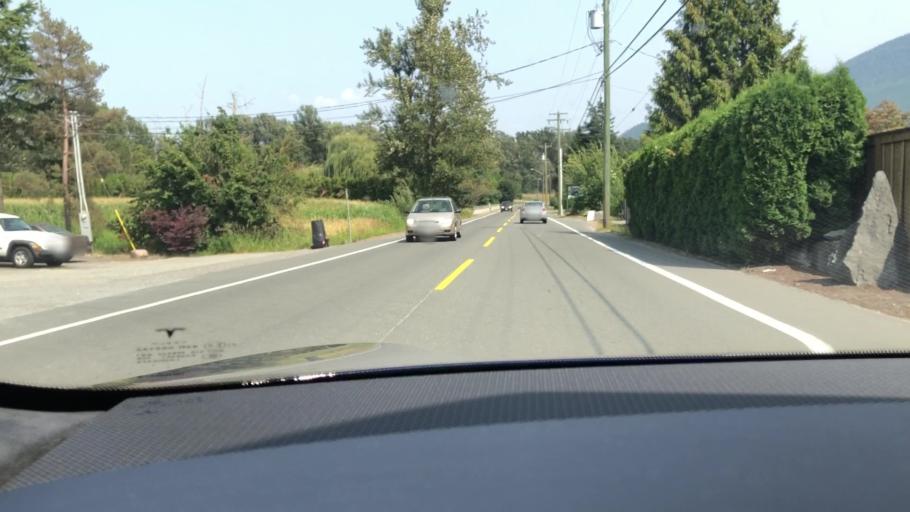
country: CA
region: British Columbia
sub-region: Fraser Valley Regional District
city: Chilliwack
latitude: 49.0892
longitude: -122.0712
